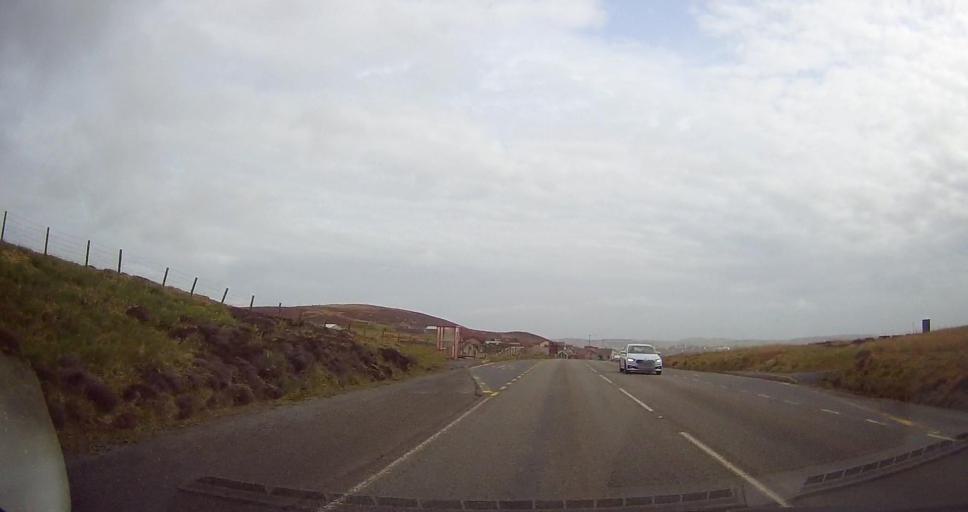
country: GB
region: Scotland
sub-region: Shetland Islands
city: Lerwick
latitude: 60.1397
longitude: -1.1876
